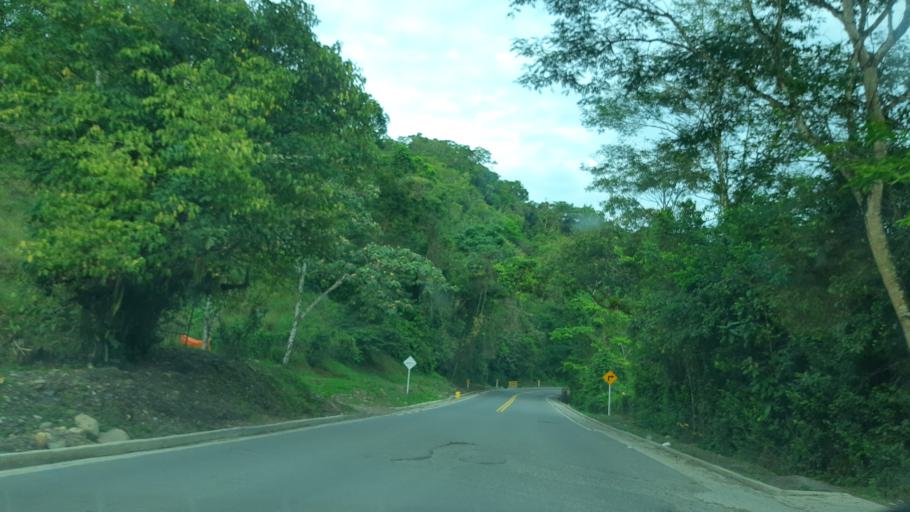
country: CO
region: Boyaca
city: San Luis de Gaceno
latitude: 4.8330
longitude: -73.1379
